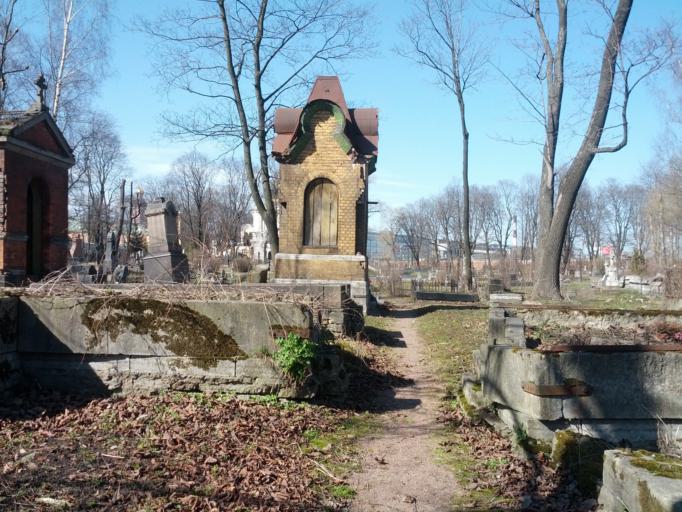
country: RU
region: St.-Petersburg
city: Centralniy
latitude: 59.9202
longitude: 30.3925
